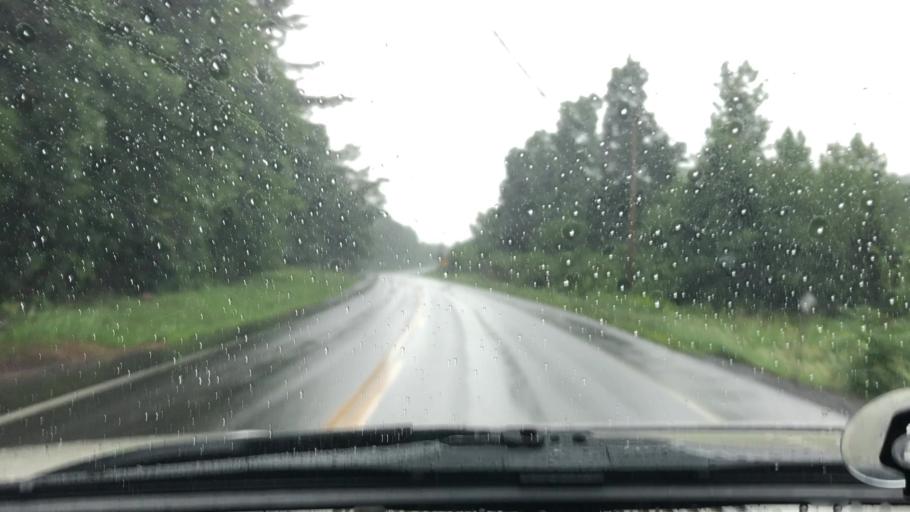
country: US
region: New York
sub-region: Greene County
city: Palenville
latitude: 42.2082
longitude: -73.9833
